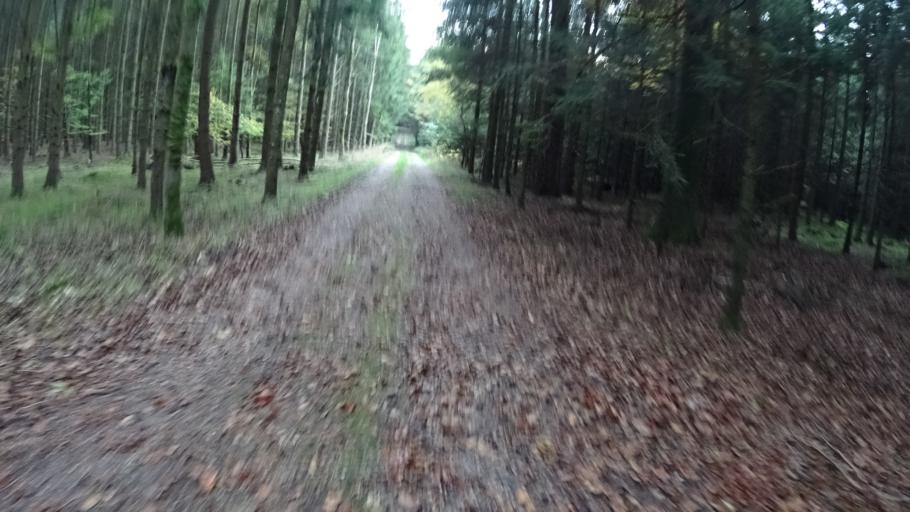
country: DE
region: Bavaria
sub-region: Upper Bavaria
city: Hitzhofen
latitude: 48.8445
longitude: 11.2970
